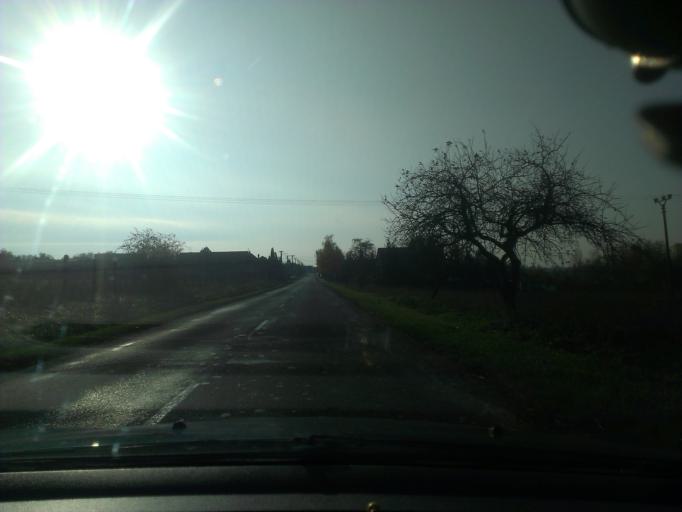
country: SK
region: Trnavsky
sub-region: Okres Trnava
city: Piestany
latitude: 48.5115
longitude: 17.9835
